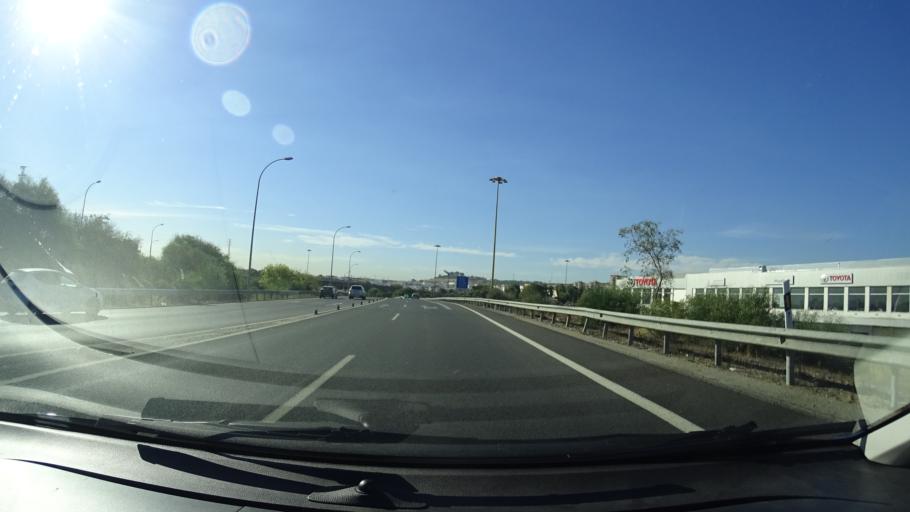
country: ES
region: Andalusia
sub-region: Provincia de Sevilla
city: Camas
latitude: 37.4124
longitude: -6.0342
